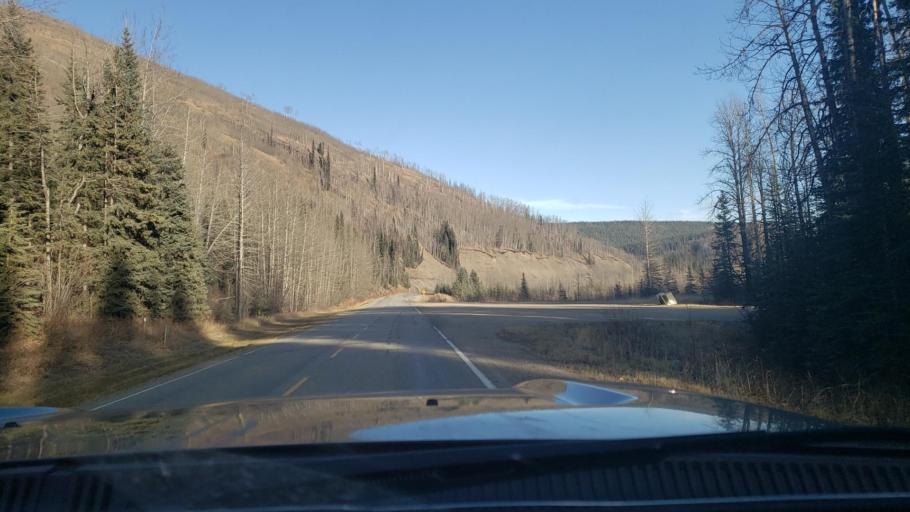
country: CA
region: British Columbia
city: Fort Nelson
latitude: 58.6574
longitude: -124.3065
